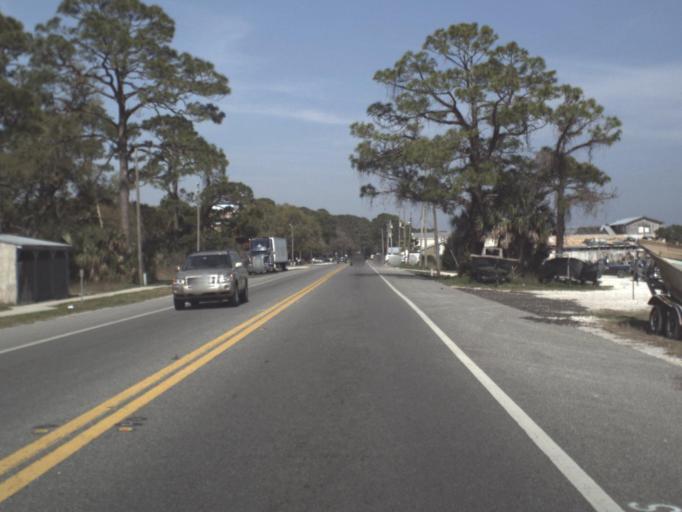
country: US
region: Florida
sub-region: Franklin County
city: Eastpoint
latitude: 29.7406
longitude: -84.8715
